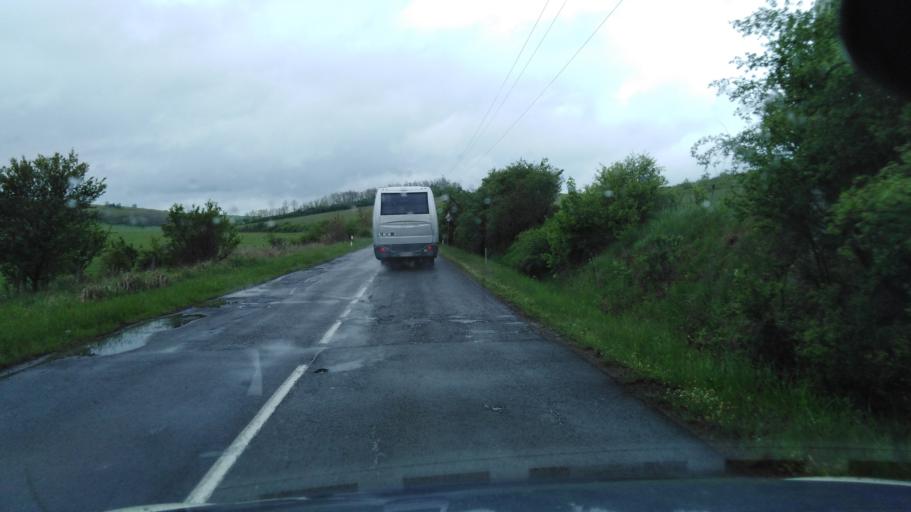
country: HU
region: Nograd
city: Rimoc
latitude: 48.0080
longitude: 19.6076
